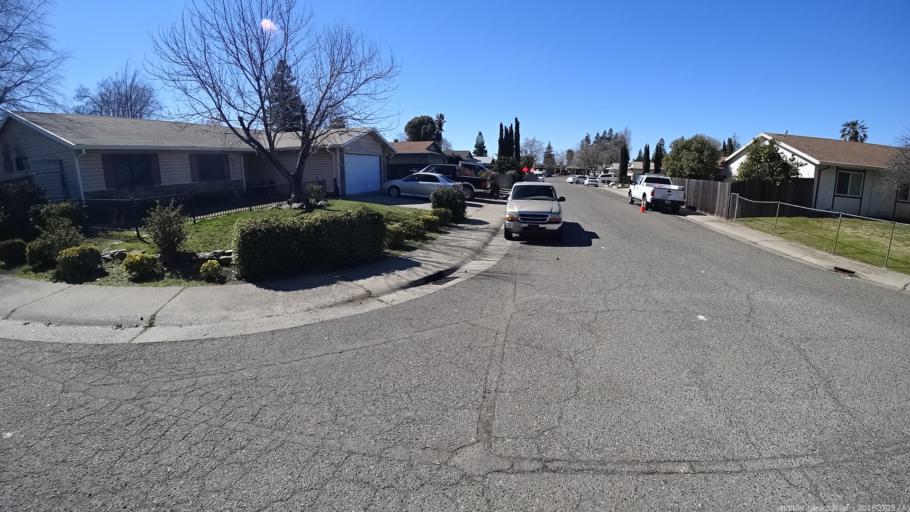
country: US
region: California
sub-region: Sacramento County
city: Florin
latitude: 38.4930
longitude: -121.3828
